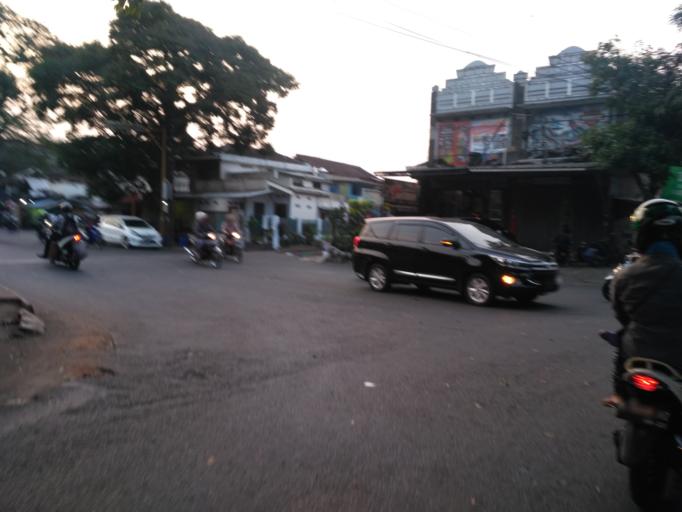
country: ID
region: East Java
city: Malang
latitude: -7.9937
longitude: 112.6335
